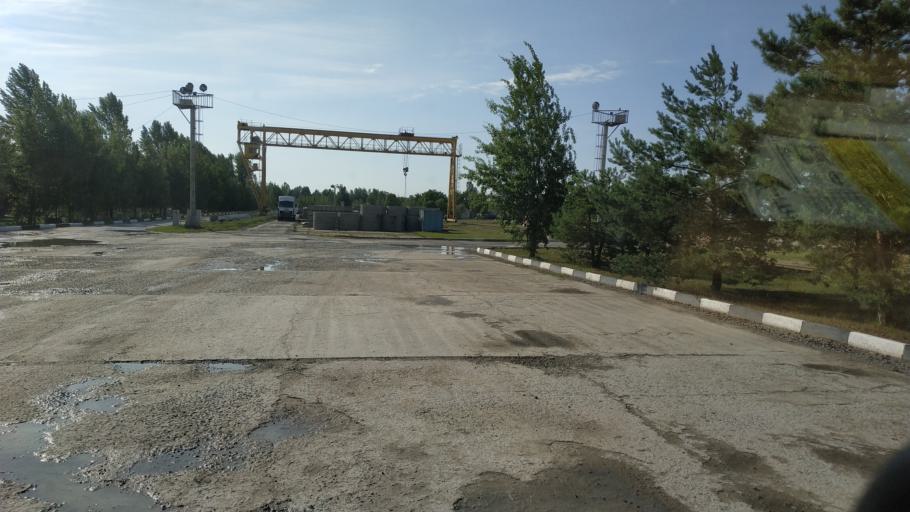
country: BY
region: Mogilev
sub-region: Mahilyowski Rayon
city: Veyno
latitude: 53.8403
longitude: 30.3836
